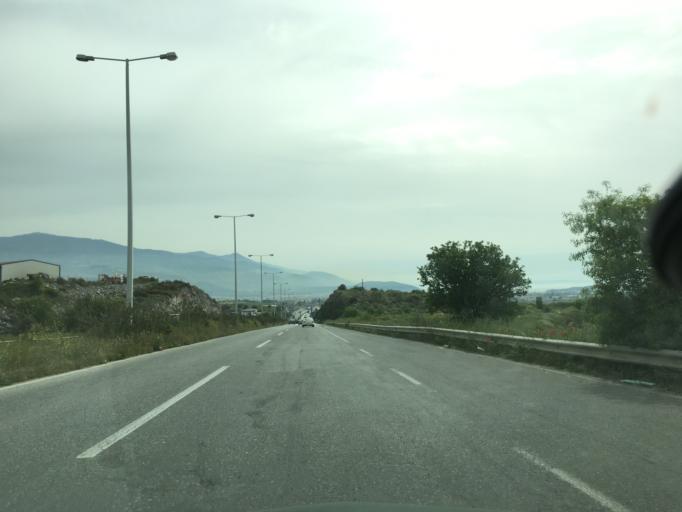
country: GR
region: Thessaly
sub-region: Nomos Magnisias
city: Nea Ionia
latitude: 39.3772
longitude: 22.8854
